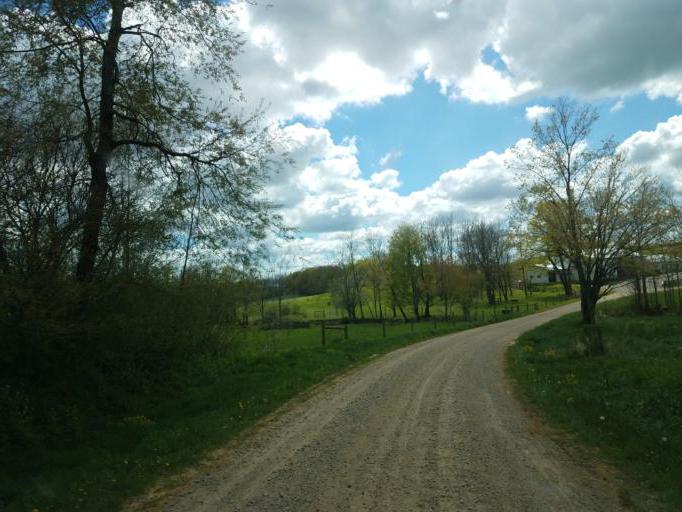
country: US
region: Ohio
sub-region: Knox County
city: Gambier
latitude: 40.5046
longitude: -82.3871
